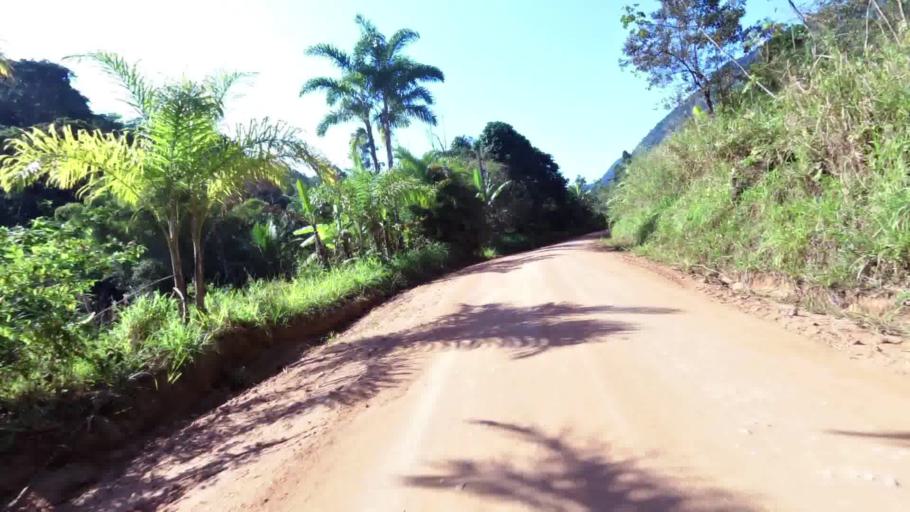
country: BR
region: Espirito Santo
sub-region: Alfredo Chaves
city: Alfredo Chaves
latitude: -20.5559
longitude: -40.7285
